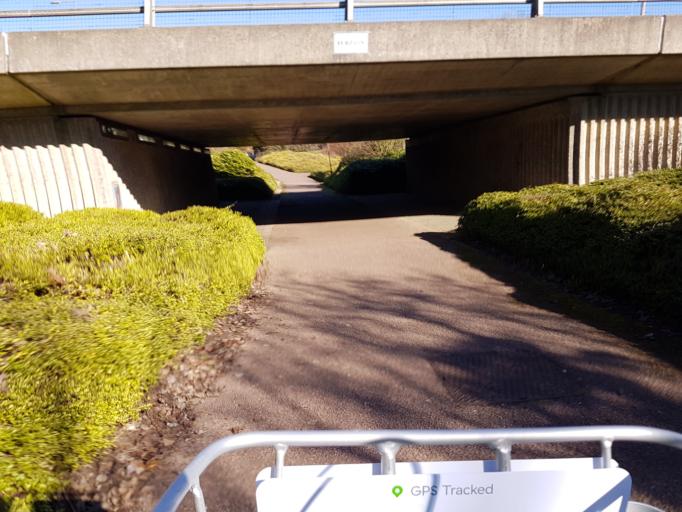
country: GB
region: England
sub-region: Buckinghamshire
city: Newton Longville
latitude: 52.0039
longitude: -0.7673
